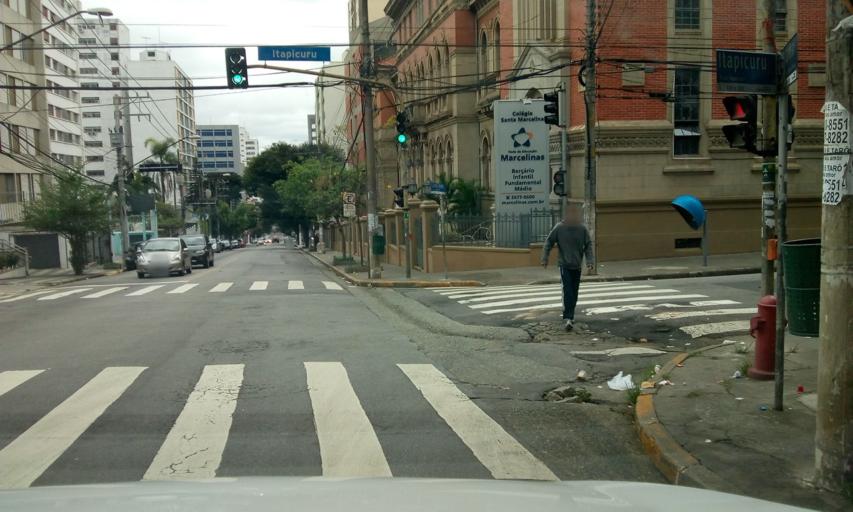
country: BR
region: Sao Paulo
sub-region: Sao Paulo
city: Sao Paulo
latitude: -23.5364
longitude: -46.6672
